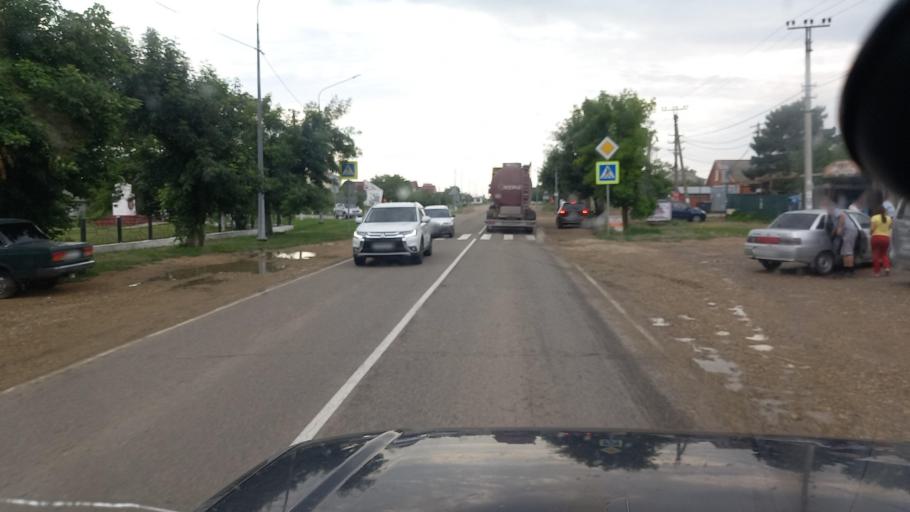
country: RU
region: Krasnodarskiy
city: Akhtanizovskaya
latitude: 45.3480
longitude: 37.1313
